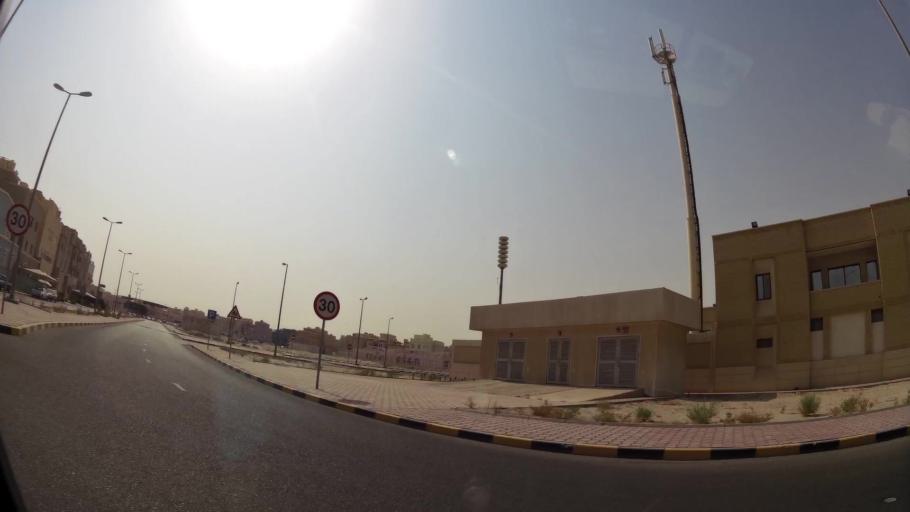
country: KW
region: Muhafazat al Jahra'
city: Al Jahra'
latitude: 29.3312
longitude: 47.7750
